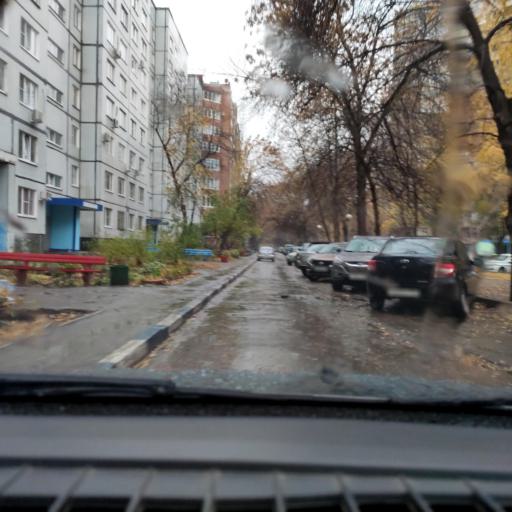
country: RU
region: Samara
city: Tol'yatti
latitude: 53.5324
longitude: 49.3090
